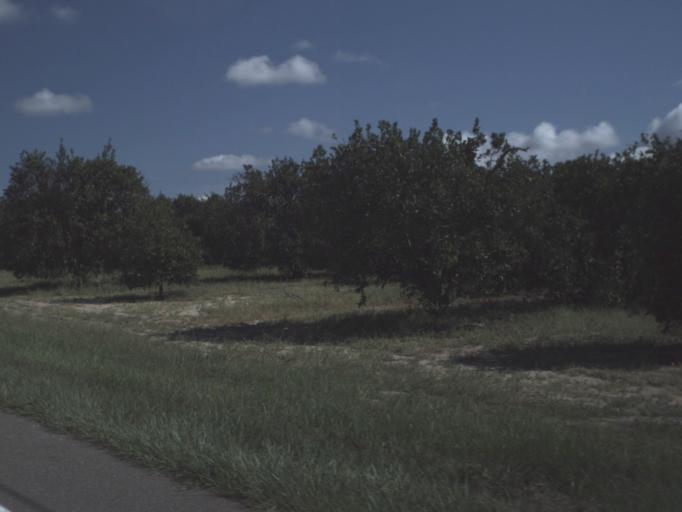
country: US
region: Florida
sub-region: Polk County
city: Babson Park
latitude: 27.7912
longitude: -81.5389
